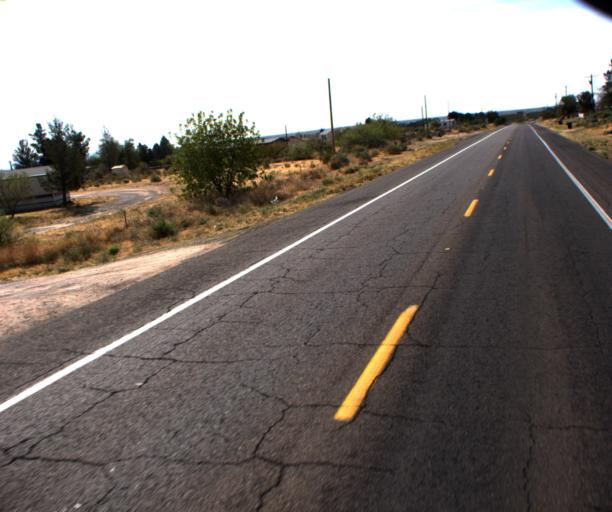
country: US
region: Arizona
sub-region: Graham County
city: Swift Trail Junction
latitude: 32.7249
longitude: -109.7120
